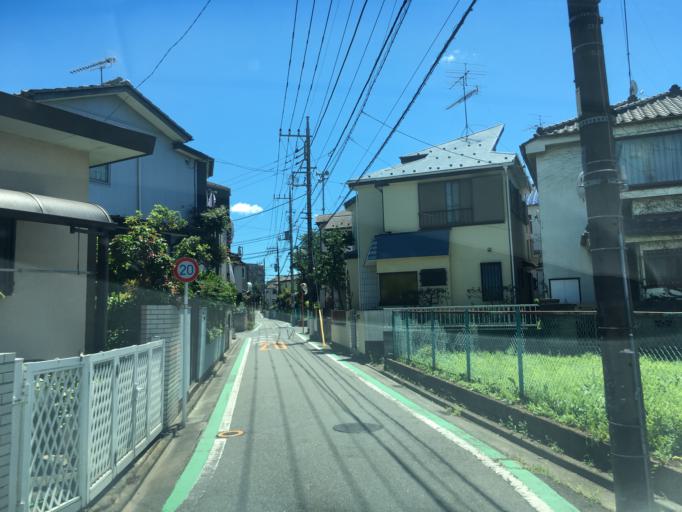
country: JP
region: Tokyo
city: Higashimurayama-shi
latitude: 35.7507
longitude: 139.4569
